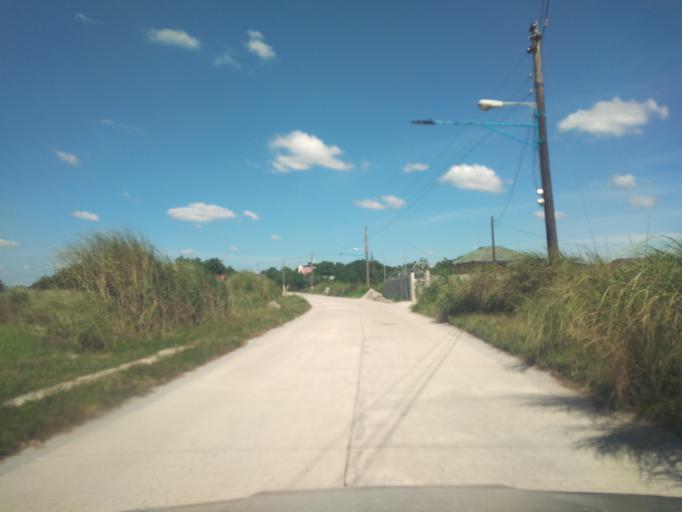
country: PH
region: Central Luzon
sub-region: Province of Pampanga
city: Balas
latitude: 15.0492
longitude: 120.6121
